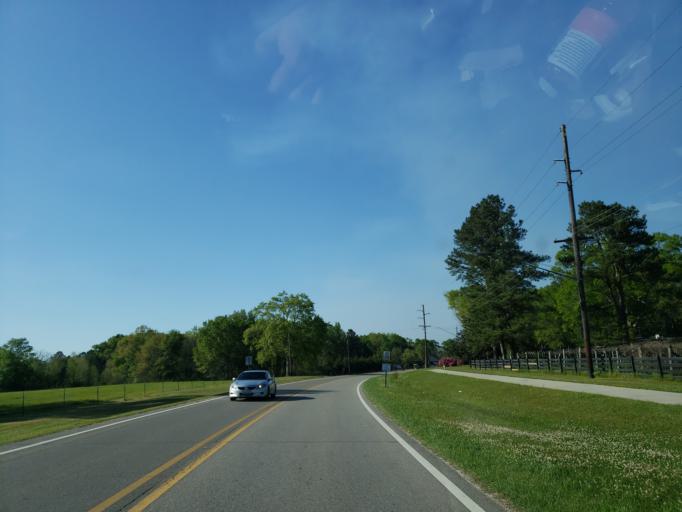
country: US
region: Mississippi
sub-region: Perry County
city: Richton
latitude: 31.3393
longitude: -88.9362
